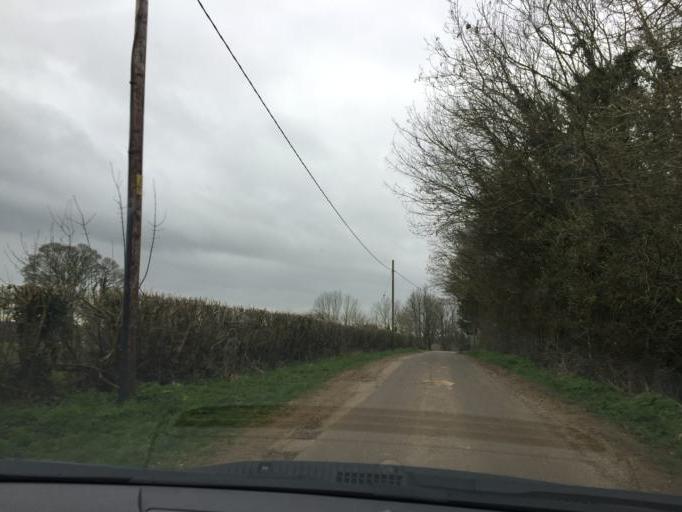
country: GB
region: England
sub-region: Oxfordshire
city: Deddington
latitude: 51.9422
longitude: -1.3681
